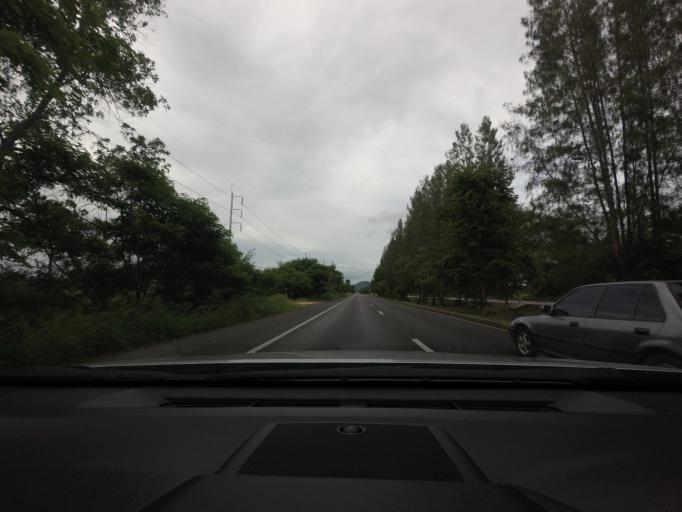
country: TH
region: Prachuap Khiri Khan
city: Hua Hin
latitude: 12.6583
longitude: 99.8742
